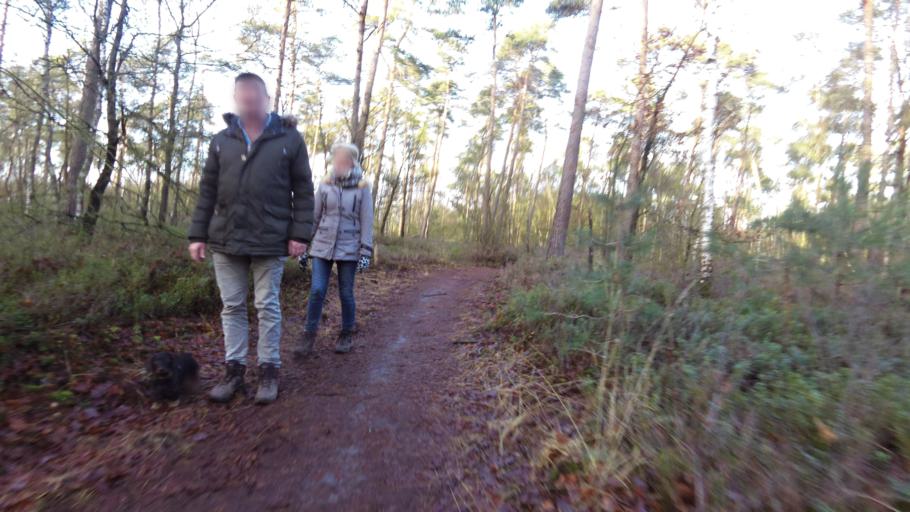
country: NL
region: Gelderland
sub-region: Gemeente Epe
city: Vaassen
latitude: 52.2958
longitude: 5.9242
